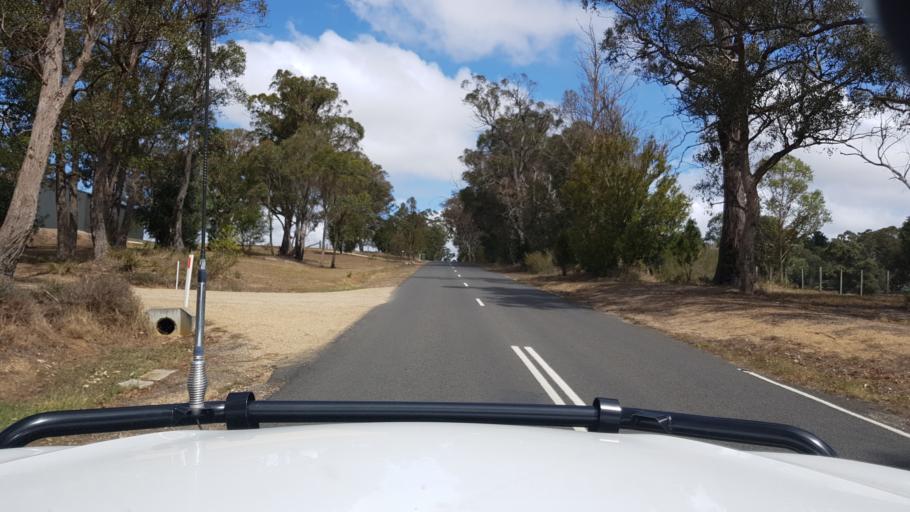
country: AU
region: Victoria
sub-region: East Gippsland
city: Bairnsdale
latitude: -37.7793
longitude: 147.6037
